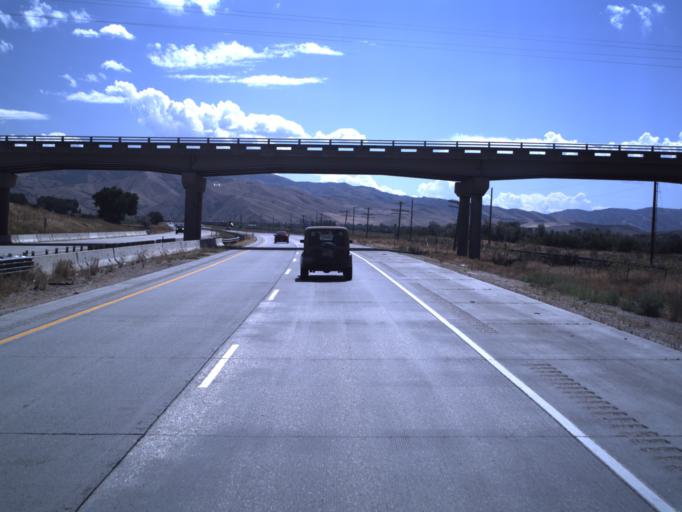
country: US
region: Utah
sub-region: Morgan County
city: Morgan
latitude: 41.0669
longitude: -111.7122
